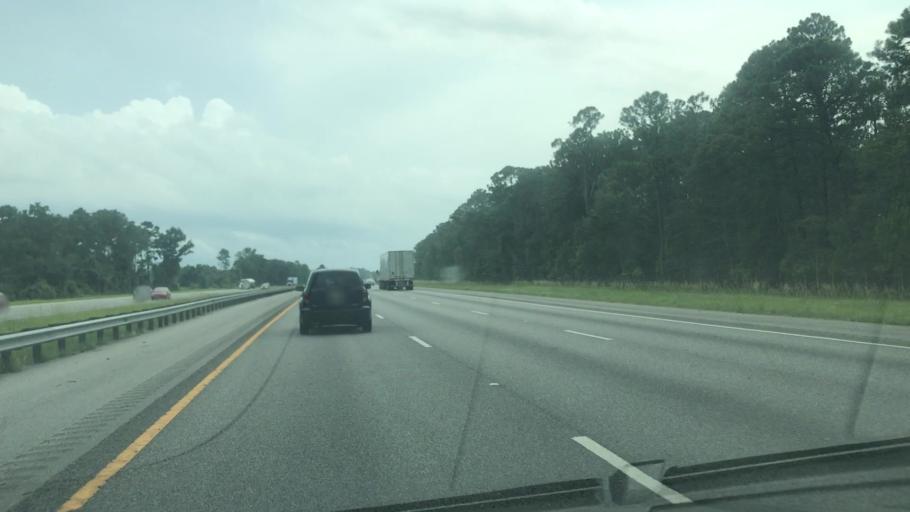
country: US
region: Georgia
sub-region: Glynn County
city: Dock Junction
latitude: 31.1821
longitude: -81.5448
